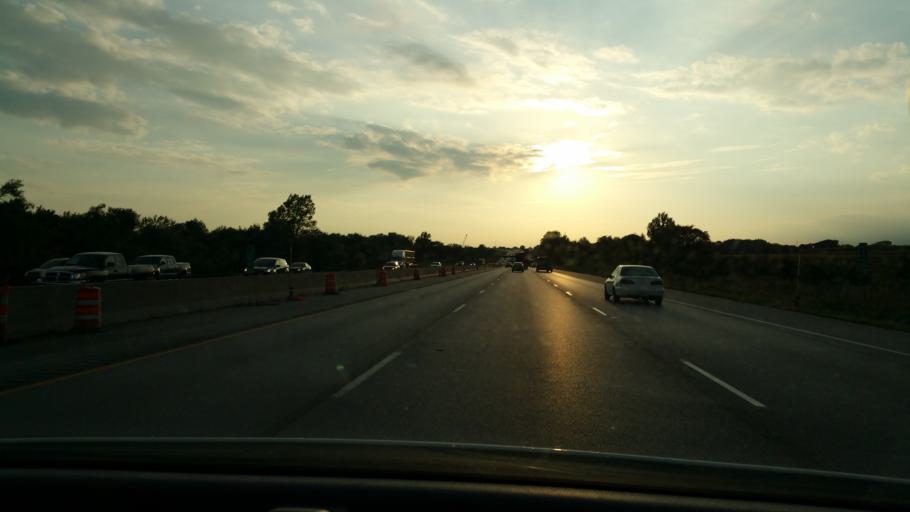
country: US
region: Iowa
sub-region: Polk County
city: Urbandale
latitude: 41.6520
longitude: -93.7450
